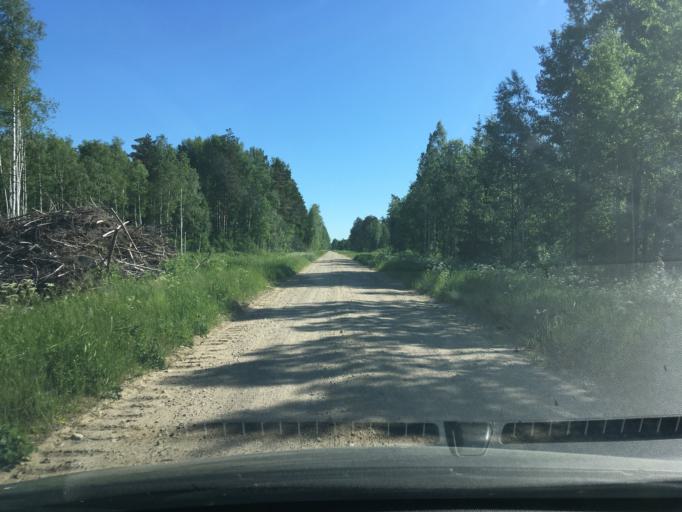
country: EE
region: Laeaene
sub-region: Lihula vald
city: Lihula
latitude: 58.6414
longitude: 23.7685
